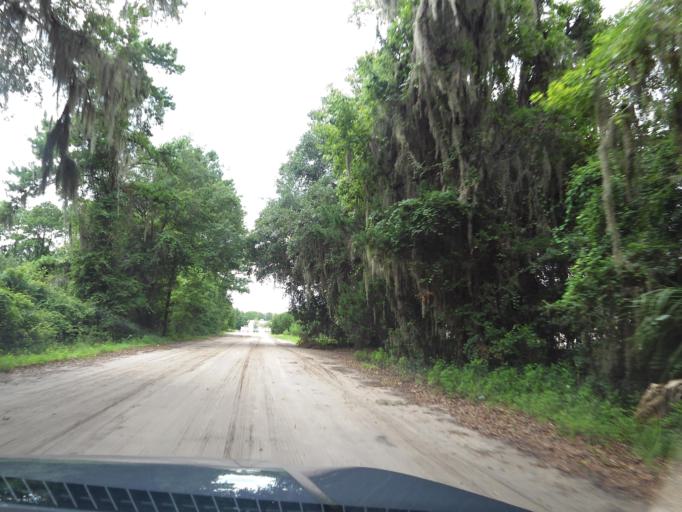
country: US
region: Georgia
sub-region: Camden County
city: Kingsland
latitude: 30.7834
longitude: -81.6450
